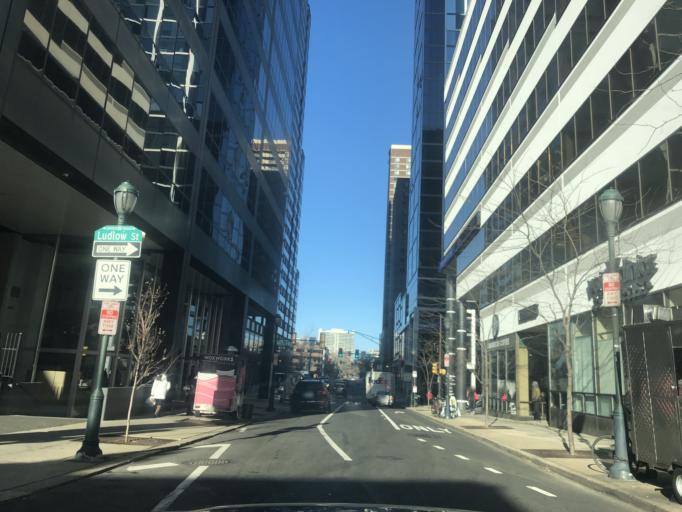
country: US
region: Pennsylvania
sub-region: Philadelphia County
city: Philadelphia
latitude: 39.9529
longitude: -75.1733
